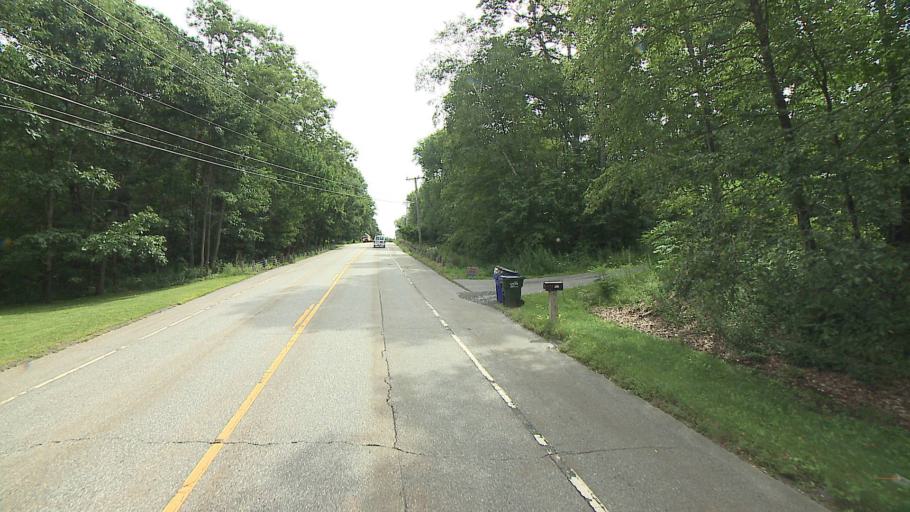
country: US
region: Connecticut
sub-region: Litchfield County
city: New Preston
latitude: 41.7434
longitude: -73.3763
